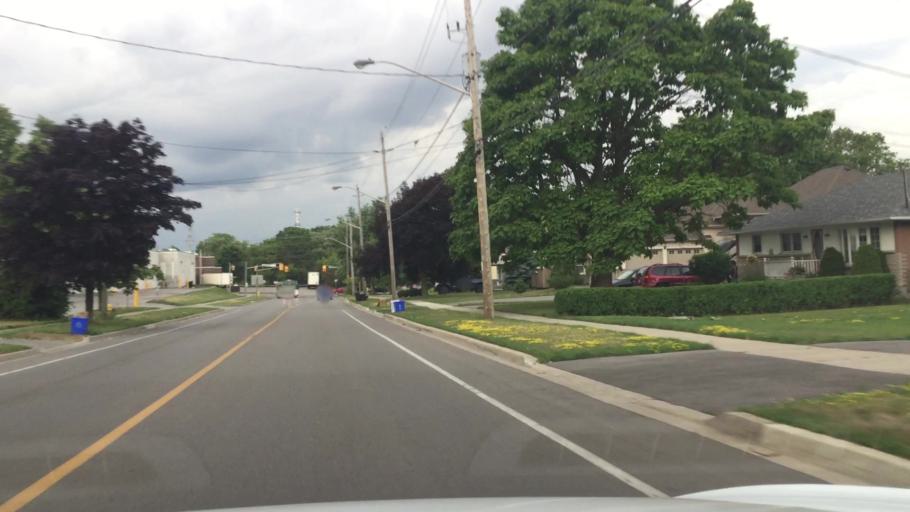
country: CA
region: Ontario
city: Oshawa
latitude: 43.9091
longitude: -78.8121
